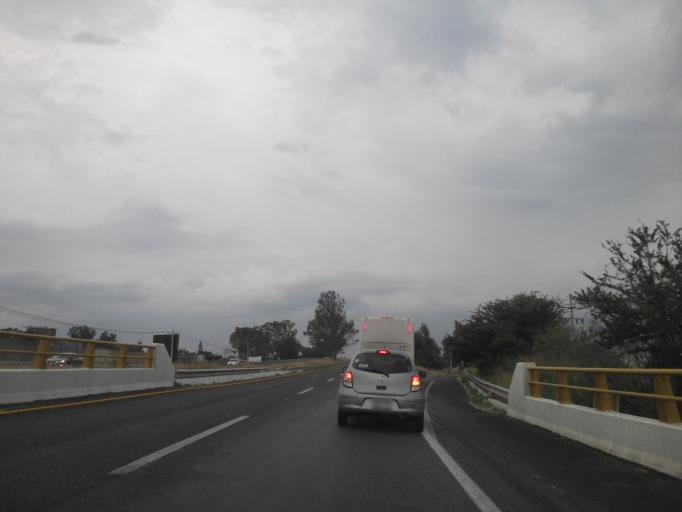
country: MX
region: Jalisco
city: Zapotlanejo
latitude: 20.6164
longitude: -103.0760
